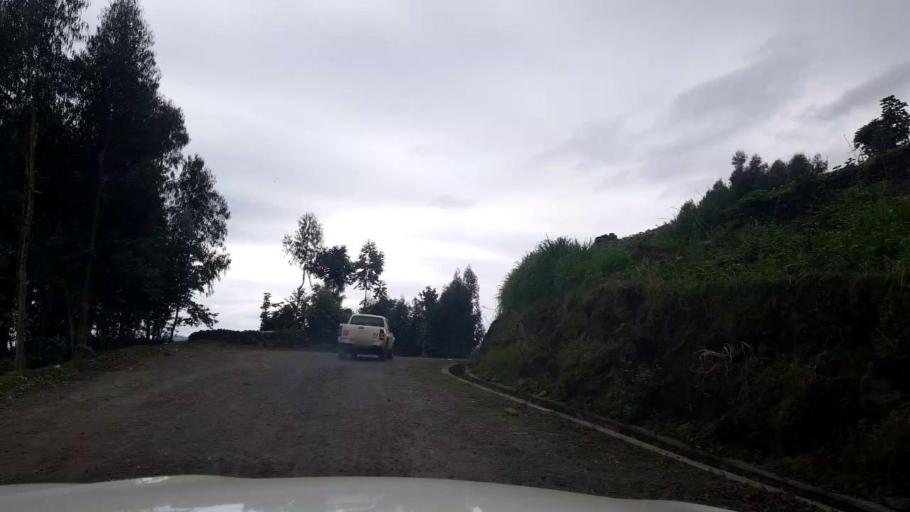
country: RW
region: Northern Province
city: Musanze
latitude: -1.5022
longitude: 29.5335
